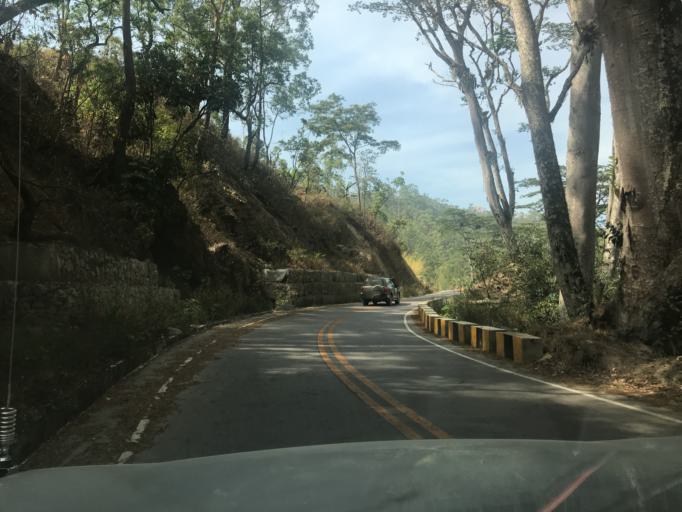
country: TL
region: Aileu
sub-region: Aileu Villa
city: Aileu
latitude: -8.6697
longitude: 125.5572
